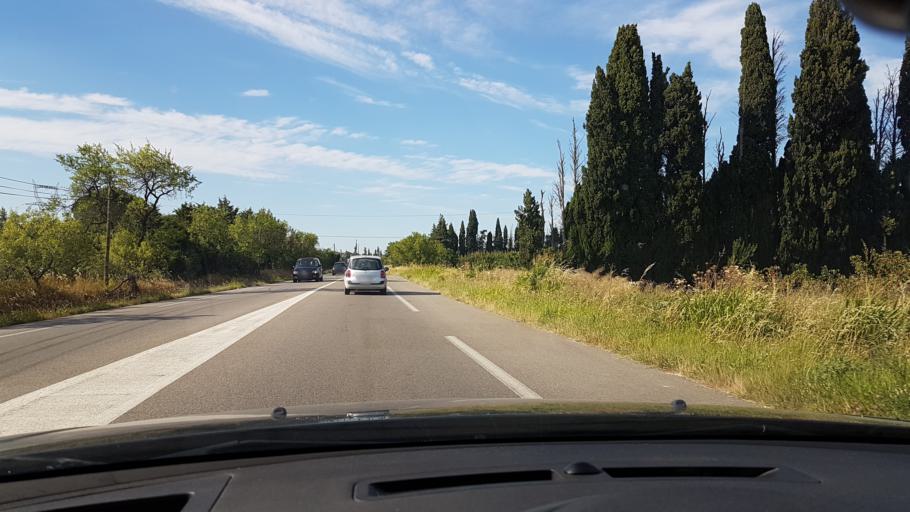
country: FR
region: Provence-Alpes-Cote d'Azur
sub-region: Departement des Bouches-du-Rhone
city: Graveson
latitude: 43.8609
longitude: 4.7690
